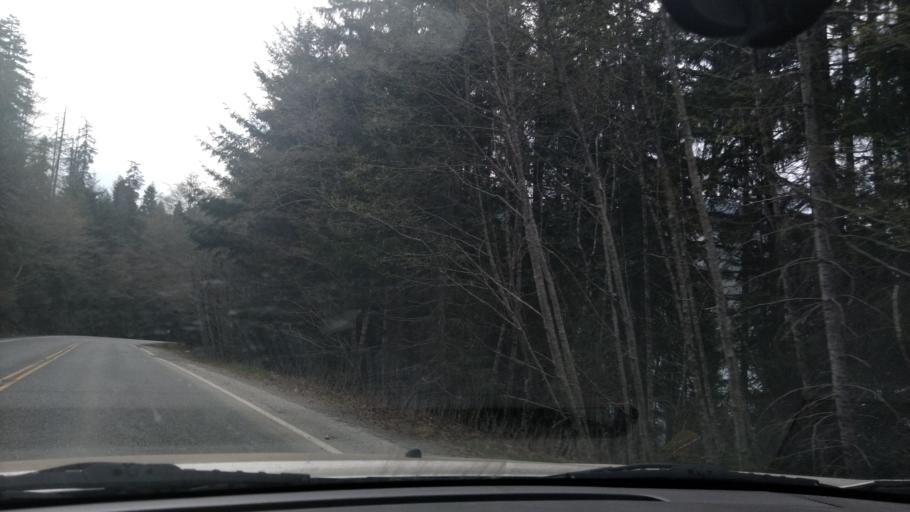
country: CA
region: British Columbia
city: Campbell River
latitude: 49.8815
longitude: -125.6832
